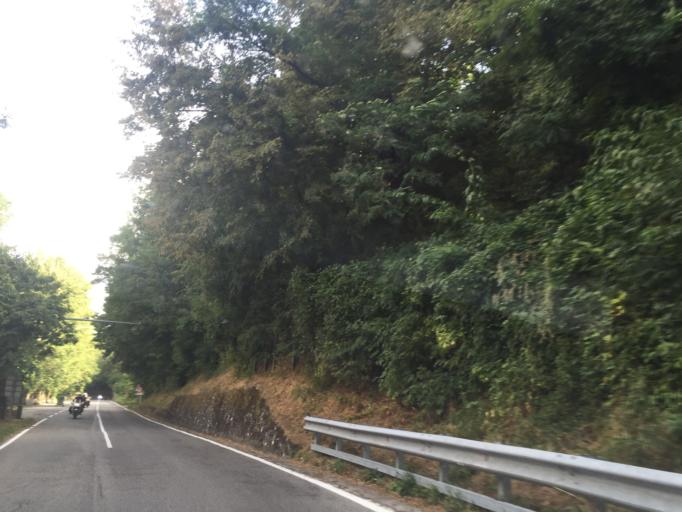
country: IT
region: Tuscany
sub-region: Provincia di Pistoia
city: Cutigliano
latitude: 44.1099
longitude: 10.7349
